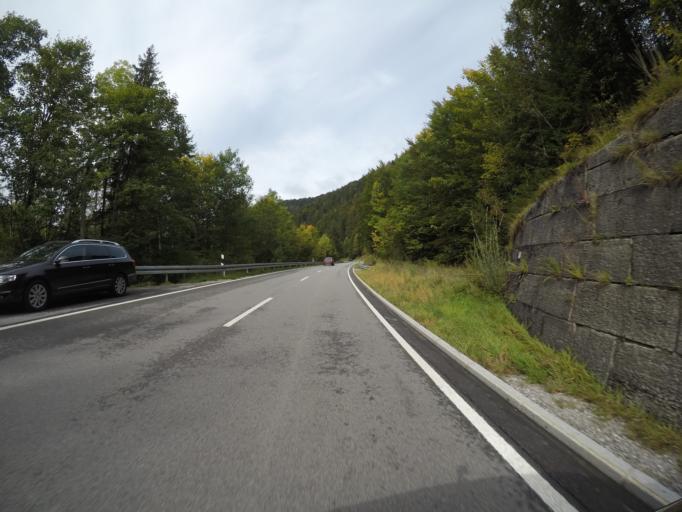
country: DE
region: Bavaria
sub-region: Upper Bavaria
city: Lenggries
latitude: 47.5837
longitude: 11.5795
